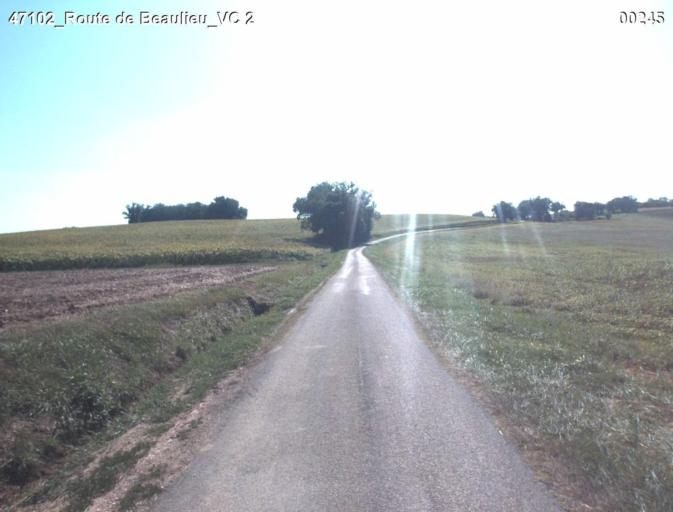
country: FR
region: Aquitaine
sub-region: Departement du Lot-et-Garonne
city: Laplume
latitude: 44.0839
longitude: 0.4456
